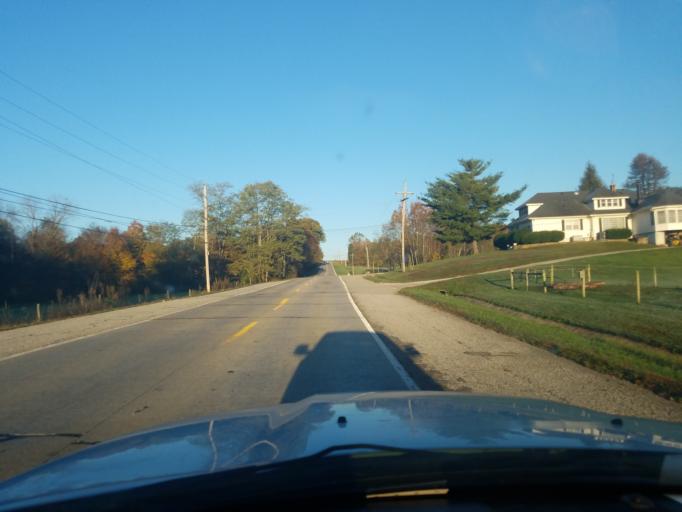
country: US
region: Indiana
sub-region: Floyd County
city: Galena
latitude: 38.3828
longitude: -86.0246
